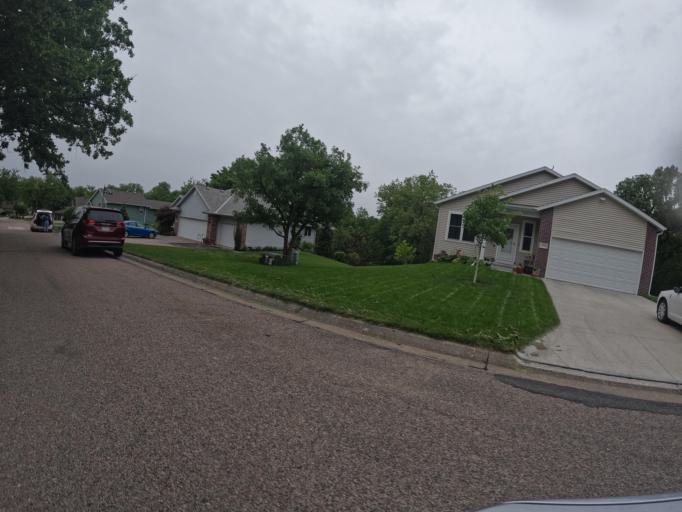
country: US
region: Nebraska
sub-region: Sarpy County
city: Offutt Air Force Base
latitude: 41.0454
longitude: -95.9740
